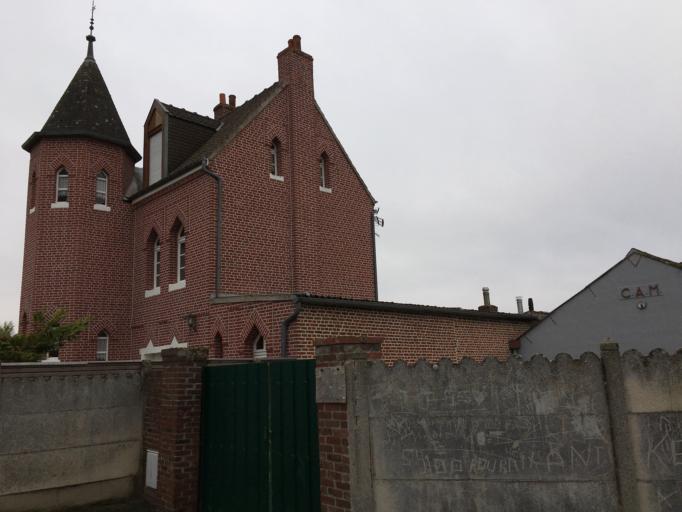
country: FR
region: Nord-Pas-de-Calais
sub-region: Departement du Nord
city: Masny
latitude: 50.3499
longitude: 3.2010
